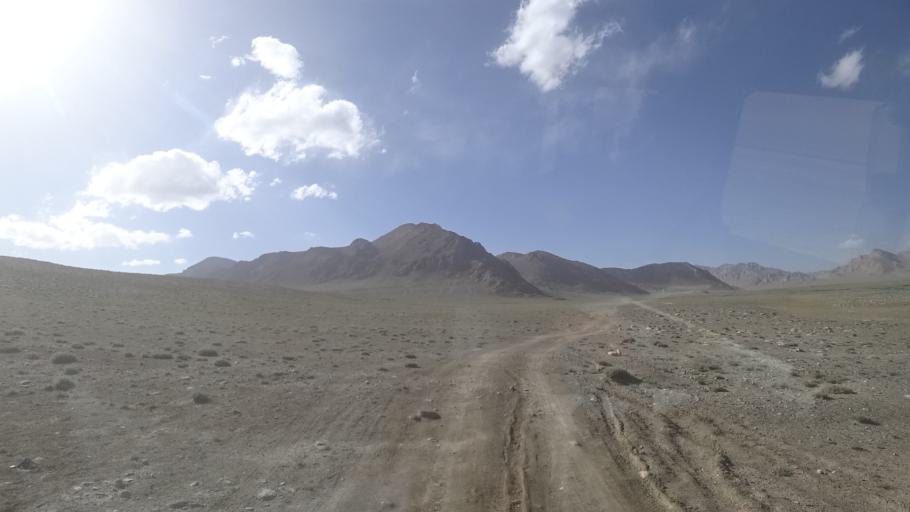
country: TJ
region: Gorno-Badakhshan
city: Murghob
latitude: 37.5855
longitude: 74.1539
